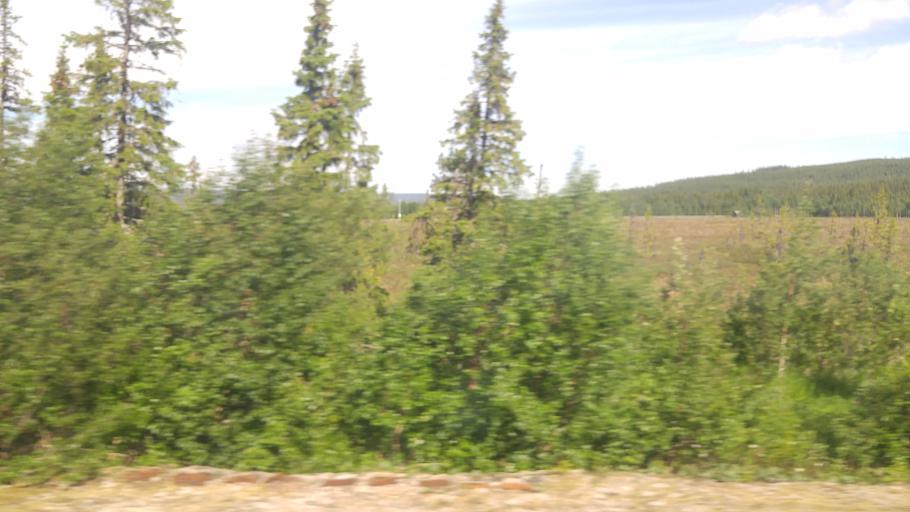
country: SE
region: Jaemtland
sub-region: Are Kommun
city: Are
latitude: 63.3647
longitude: 12.7052
